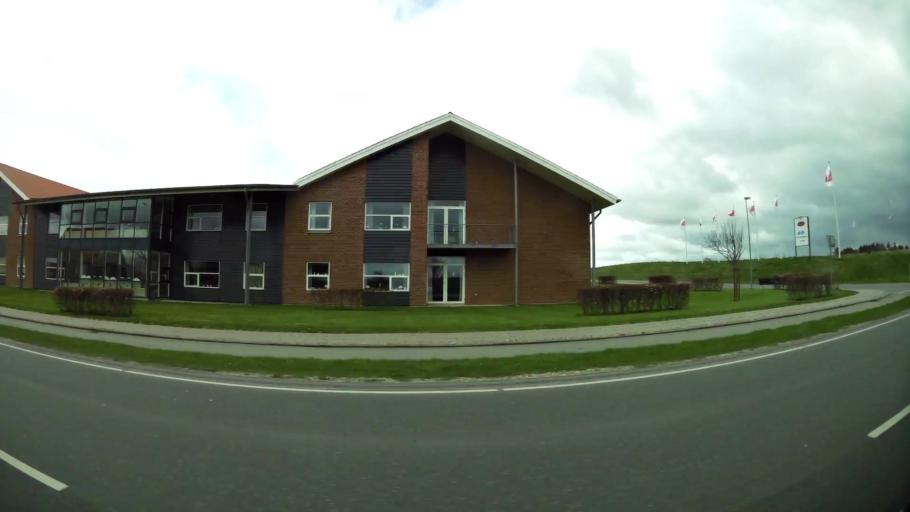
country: DK
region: North Denmark
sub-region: Thisted Kommune
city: Thisted
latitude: 56.9448
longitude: 8.6572
